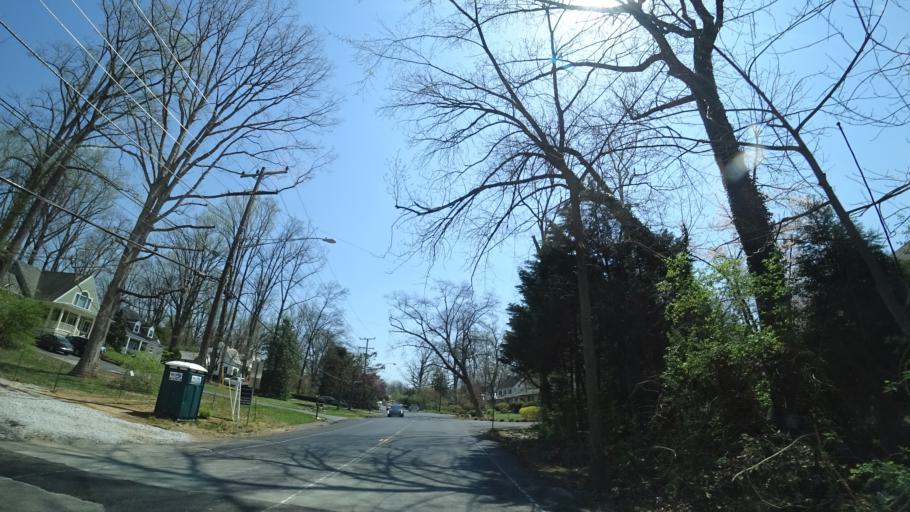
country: US
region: Maryland
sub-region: Montgomery County
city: Bethesda
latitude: 38.9905
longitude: -77.1173
